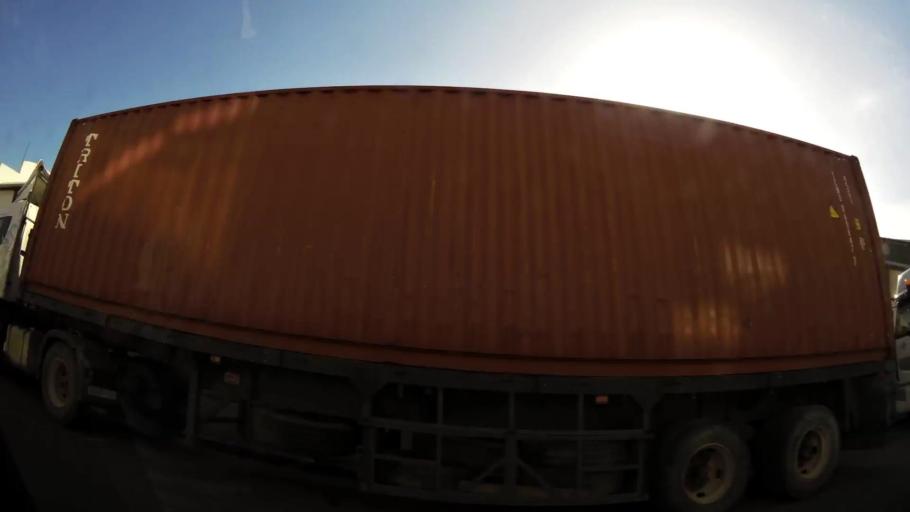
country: MA
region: Grand Casablanca
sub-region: Casablanca
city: Casablanca
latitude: 33.6028
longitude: -7.5789
